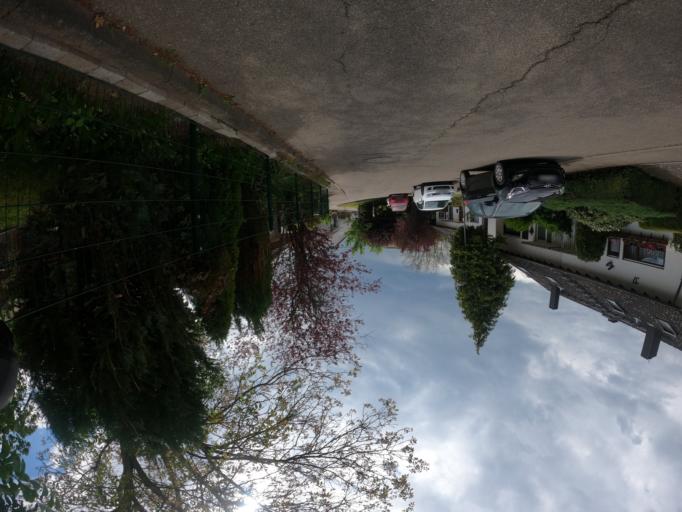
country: DE
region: Baden-Wuerttemberg
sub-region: Regierungsbezirk Stuttgart
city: Weil im Schonbuch
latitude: 48.6159
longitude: 9.0683
